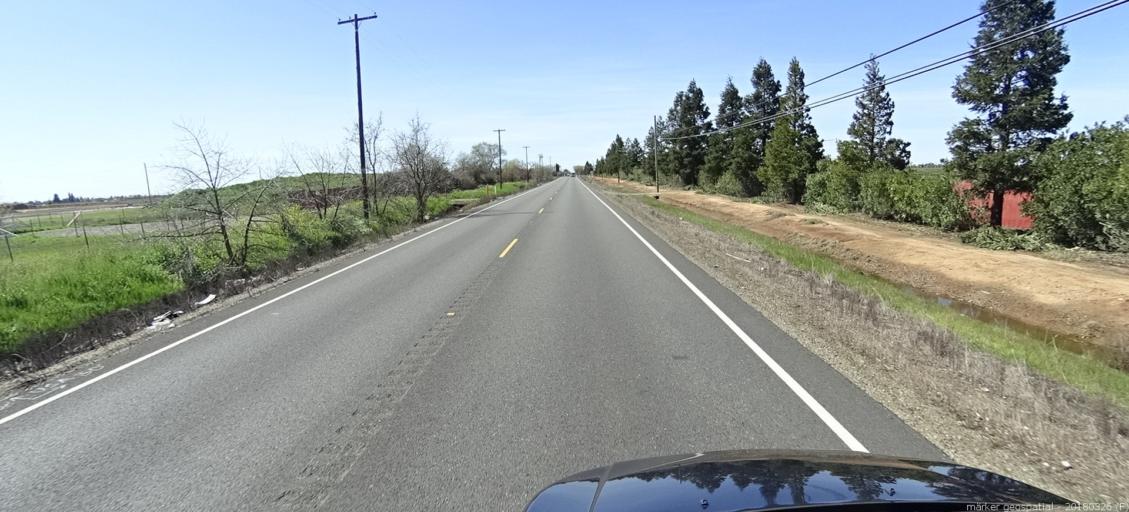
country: US
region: California
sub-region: Sacramento County
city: Rosemont
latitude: 38.5248
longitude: -121.3192
